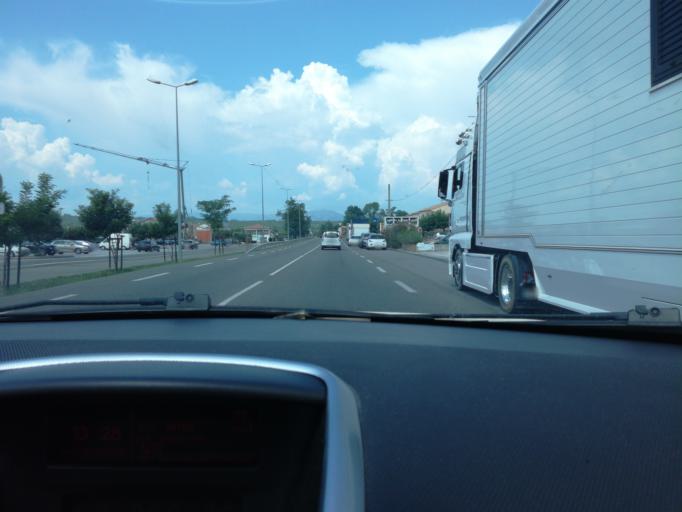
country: FR
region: Rhone-Alpes
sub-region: Departement de l'Ardeche
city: Ruoms
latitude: 44.4526
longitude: 4.3461
